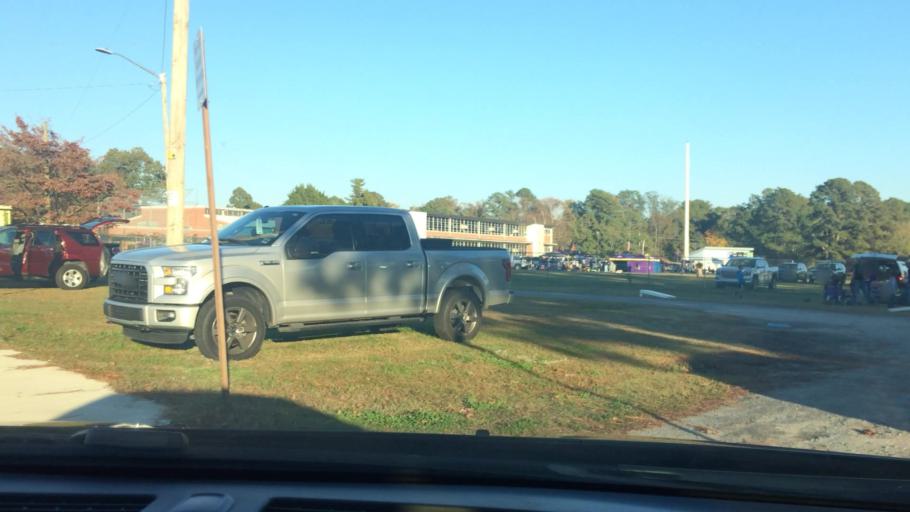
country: US
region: North Carolina
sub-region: Pitt County
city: Greenville
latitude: 35.5986
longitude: -77.3626
